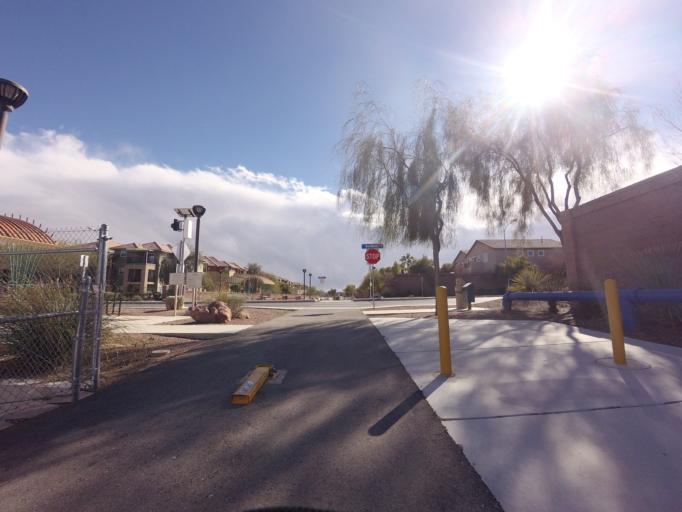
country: US
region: Nevada
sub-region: Clark County
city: North Las Vegas
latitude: 36.2545
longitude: -115.1193
